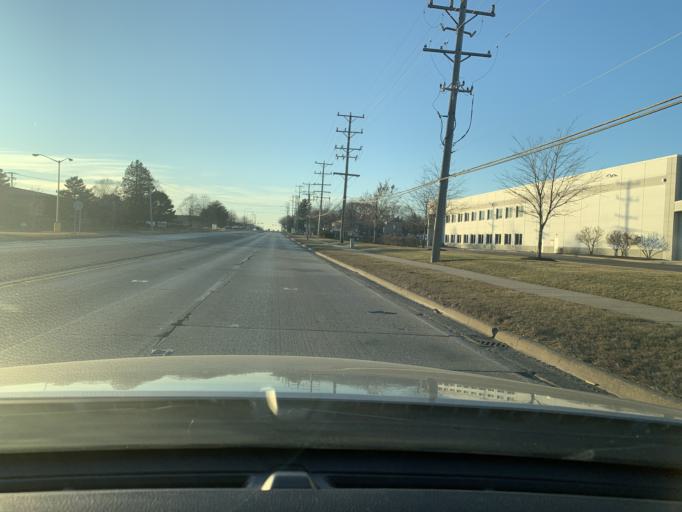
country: US
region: Illinois
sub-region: Cook County
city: Elk Grove Village
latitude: 41.9930
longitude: -87.9735
